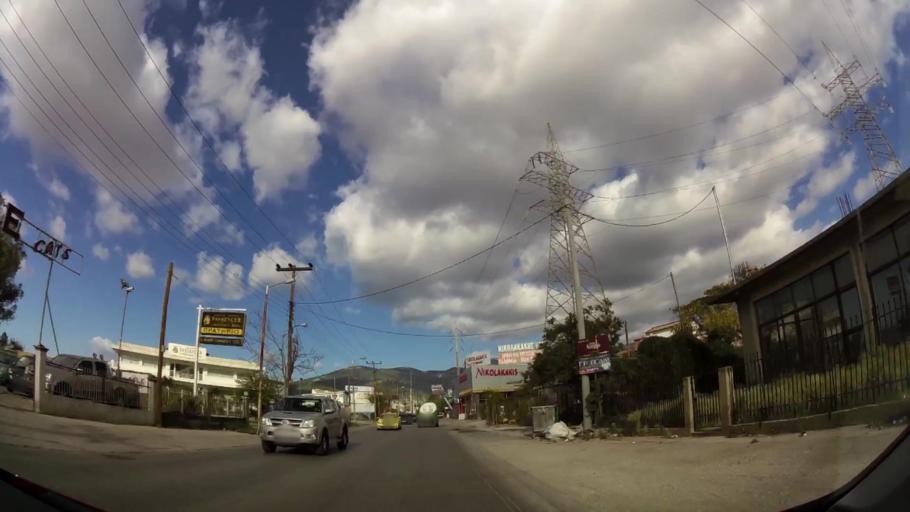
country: GR
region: Attica
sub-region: Nomarchia Anatolikis Attikis
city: Acharnes
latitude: 38.0916
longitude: 23.7560
